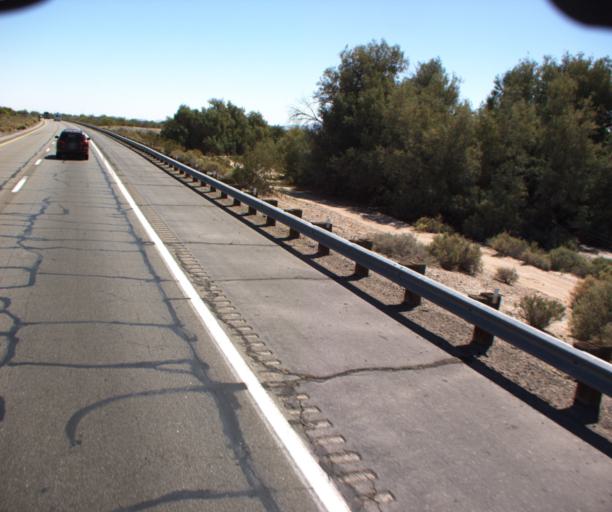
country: US
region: Arizona
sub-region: Yuma County
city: Wellton
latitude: 32.6498
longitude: -114.2142
